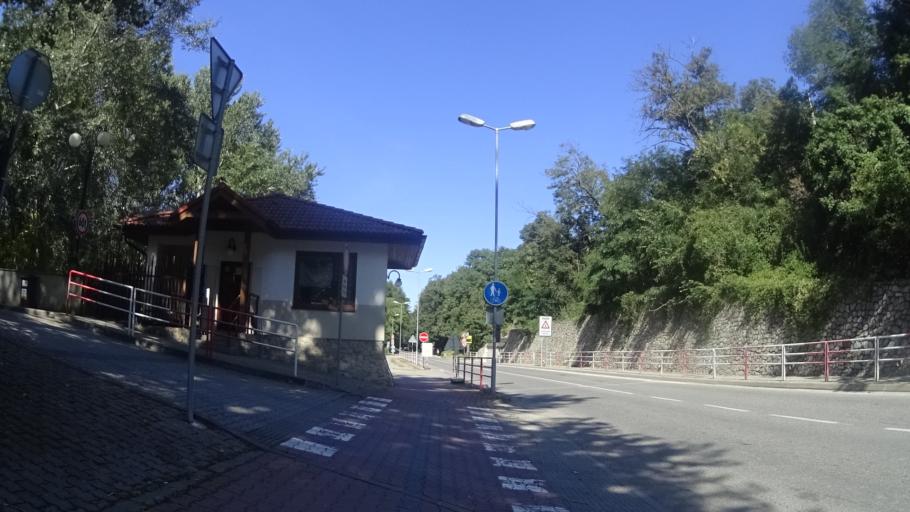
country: AT
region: Lower Austria
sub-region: Politischer Bezirk Bruck an der Leitha
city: Wolfsthal
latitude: 48.1484
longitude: 17.0451
